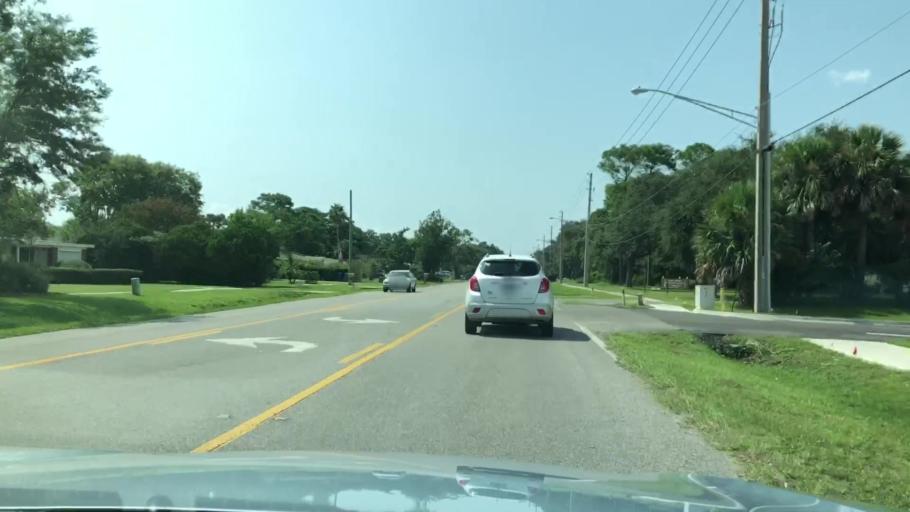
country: US
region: Florida
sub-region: Duval County
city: Atlantic Beach
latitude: 30.3230
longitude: -81.4090
